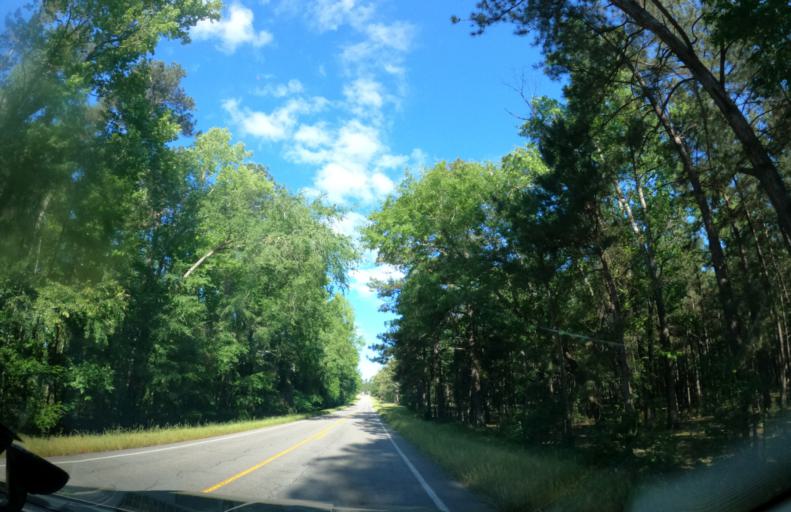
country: US
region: Georgia
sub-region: Columbia County
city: Grovetown
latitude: 33.4435
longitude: -82.2517
